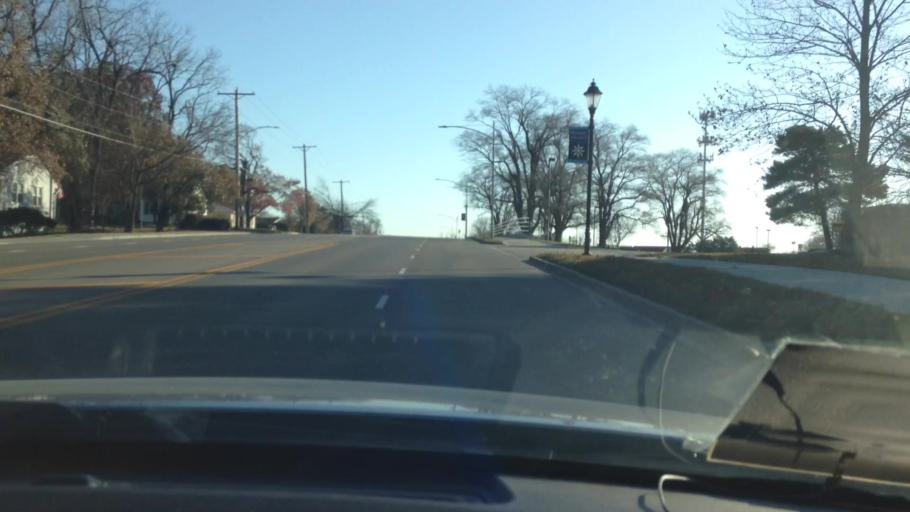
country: US
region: Kansas
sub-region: Johnson County
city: Prairie Village
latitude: 38.9922
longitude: -94.6305
